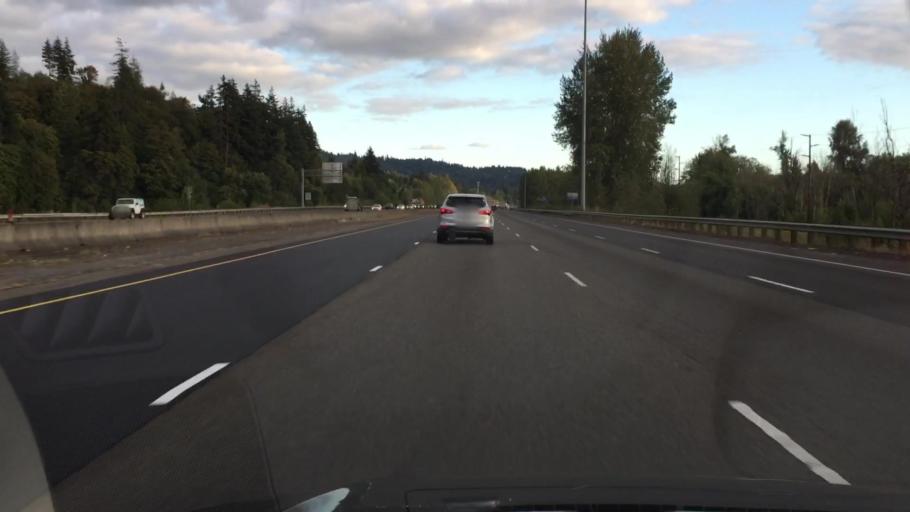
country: US
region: Washington
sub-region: Cowlitz County
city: Kelso
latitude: 46.0989
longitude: -122.8747
